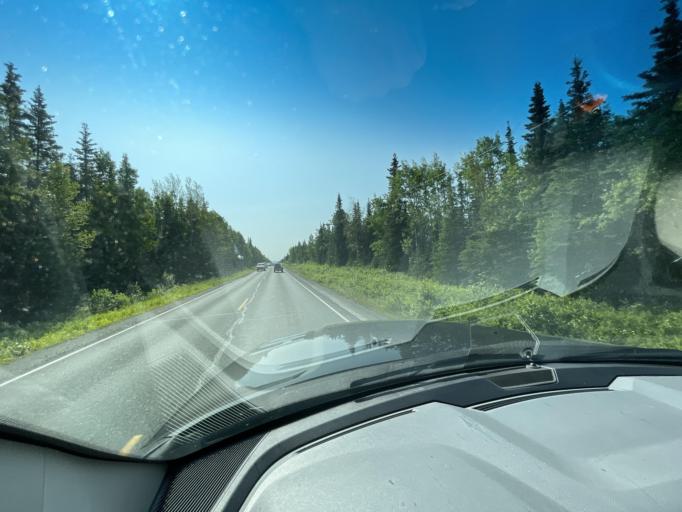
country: US
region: Alaska
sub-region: Kenai Peninsula Borough
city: Cohoe
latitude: 60.3140
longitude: -151.2944
